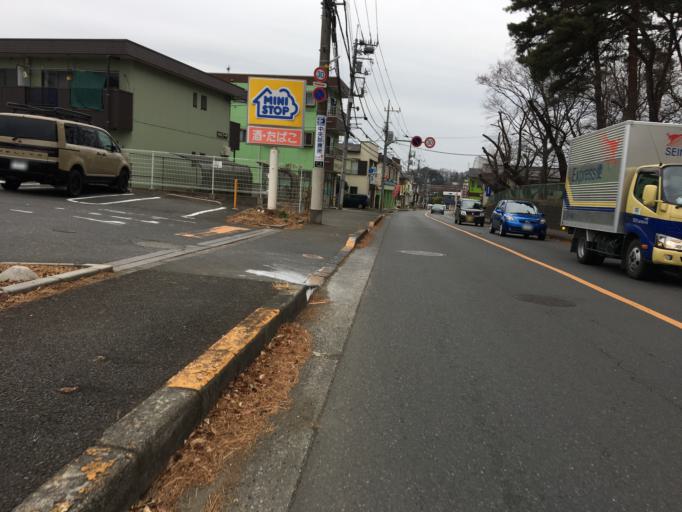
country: JP
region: Saitama
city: Oi
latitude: 35.7945
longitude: 139.5357
